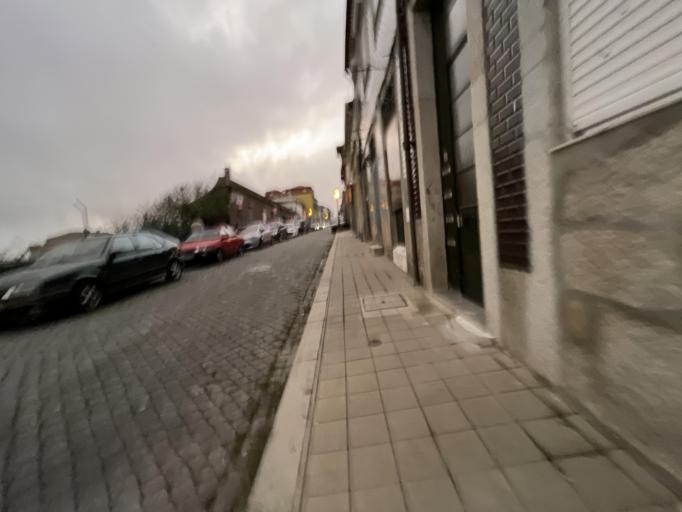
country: PT
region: Porto
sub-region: Porto
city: Porto
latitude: 41.1420
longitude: -8.5967
